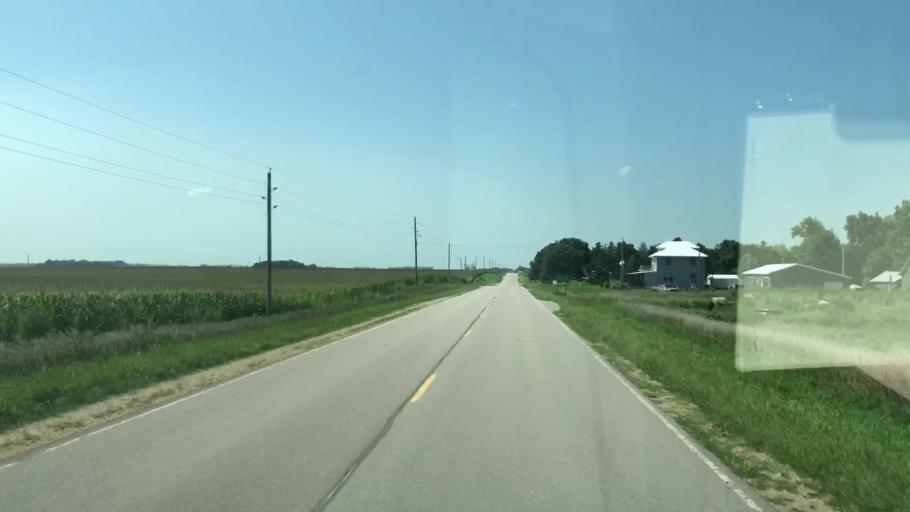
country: US
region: Iowa
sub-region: O'Brien County
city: Sheldon
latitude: 43.2443
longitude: -95.7796
